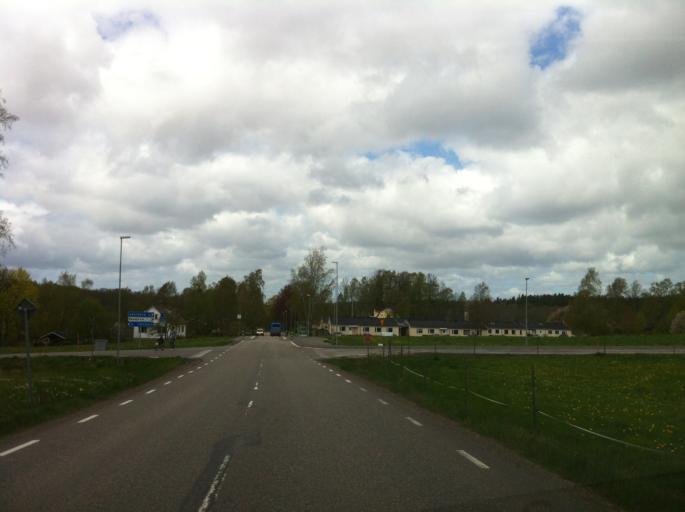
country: SE
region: Vaestra Goetaland
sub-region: Alingsas Kommun
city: Ingared
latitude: 57.8450
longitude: 12.4865
